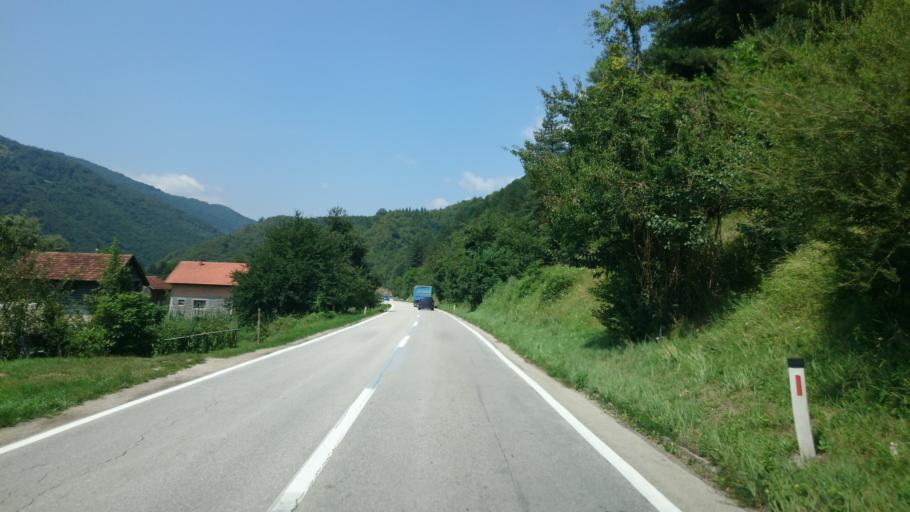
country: BA
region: Federation of Bosnia and Herzegovina
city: Donji Vakuf
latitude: 44.1790
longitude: 17.3544
